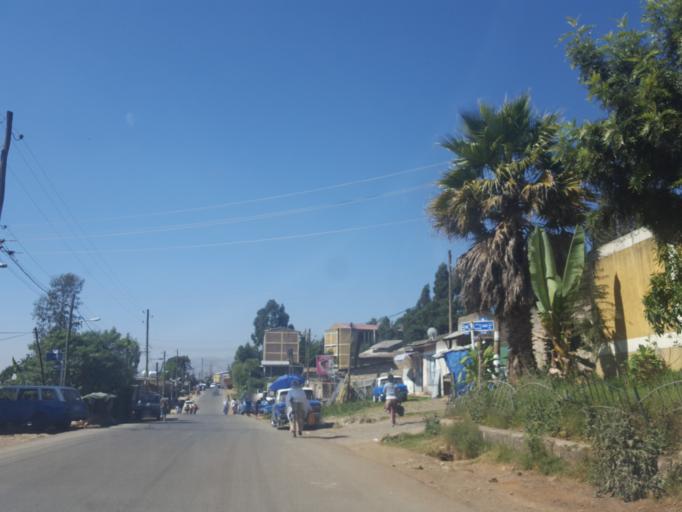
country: ET
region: Adis Abeba
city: Addis Ababa
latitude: 9.0620
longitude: 38.7420
